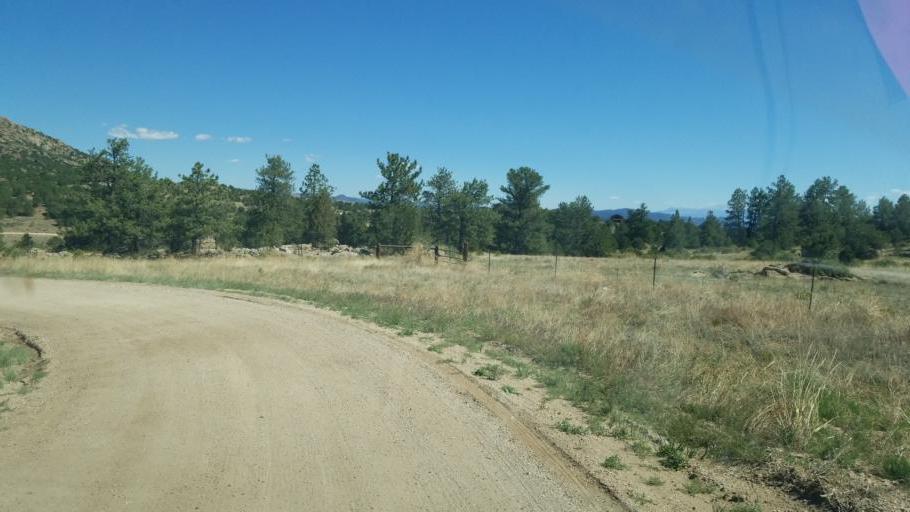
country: US
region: Colorado
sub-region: Custer County
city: Westcliffe
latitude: 38.2357
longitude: -105.4753
